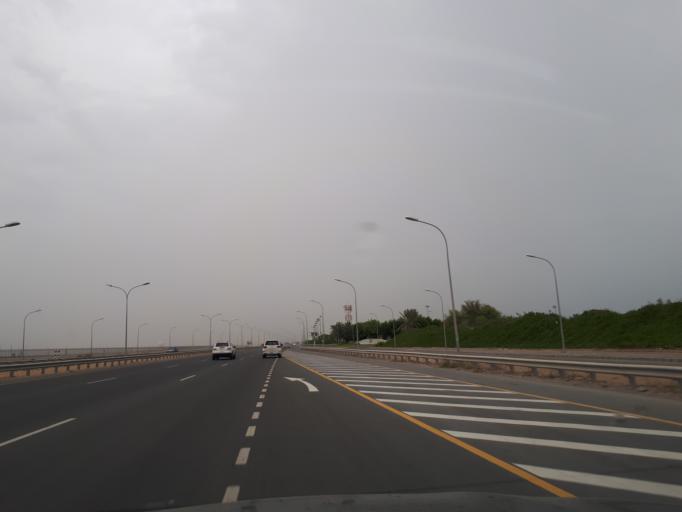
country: OM
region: Muhafazat Masqat
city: Bawshar
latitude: 23.6107
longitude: 58.3038
